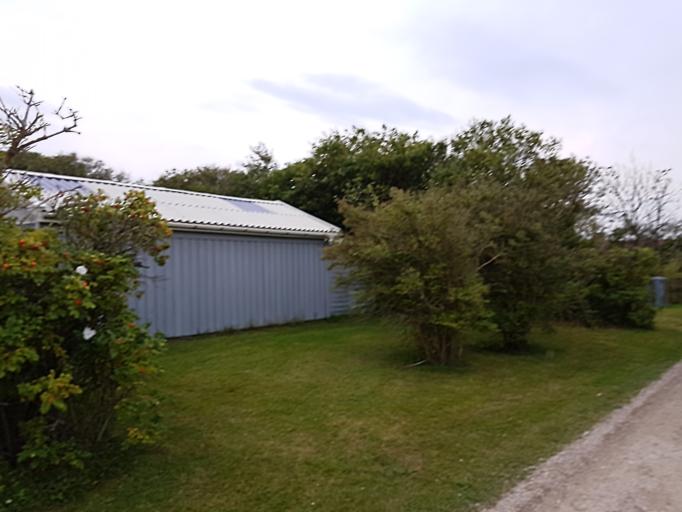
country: DK
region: Central Jutland
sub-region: Ringkobing-Skjern Kommune
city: Hvide Sande
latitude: 55.8502
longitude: 8.2858
